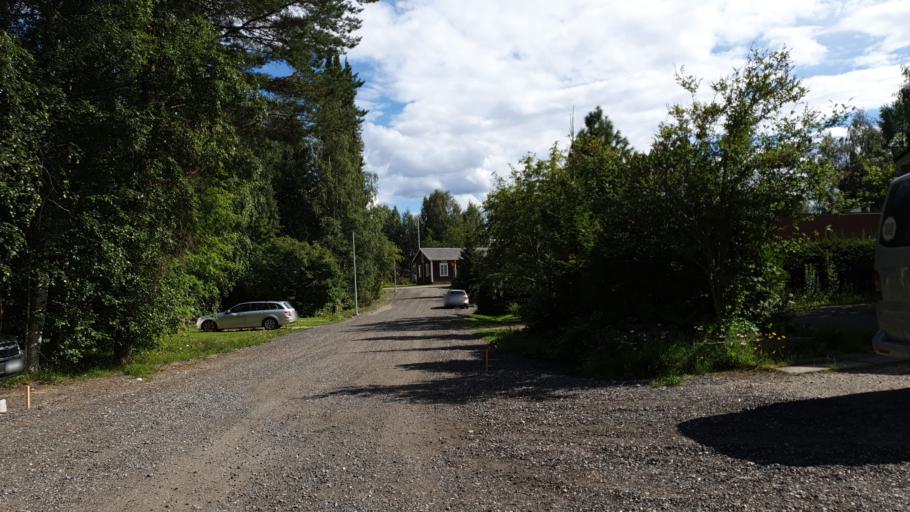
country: FI
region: Kainuu
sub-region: Kehys-Kainuu
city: Kuhmo
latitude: 64.1258
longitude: 29.5021
